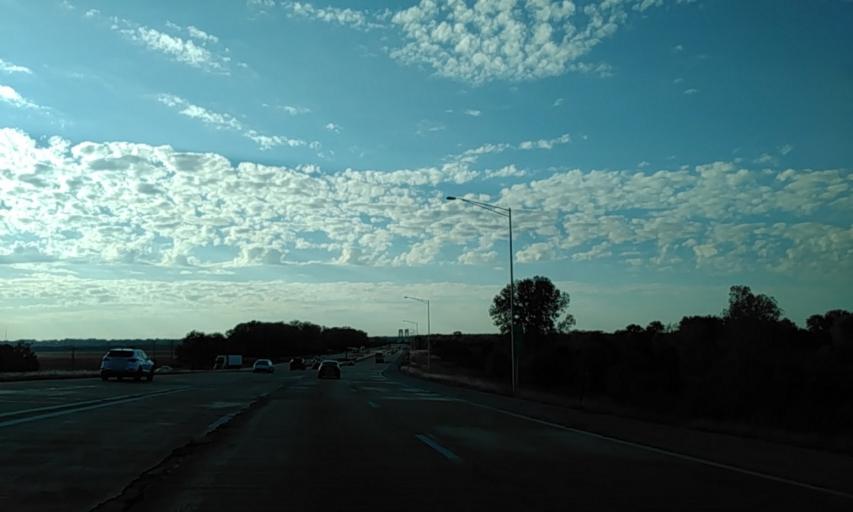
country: US
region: Illinois
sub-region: Monroe County
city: Columbia
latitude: 38.4749
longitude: -90.2349
